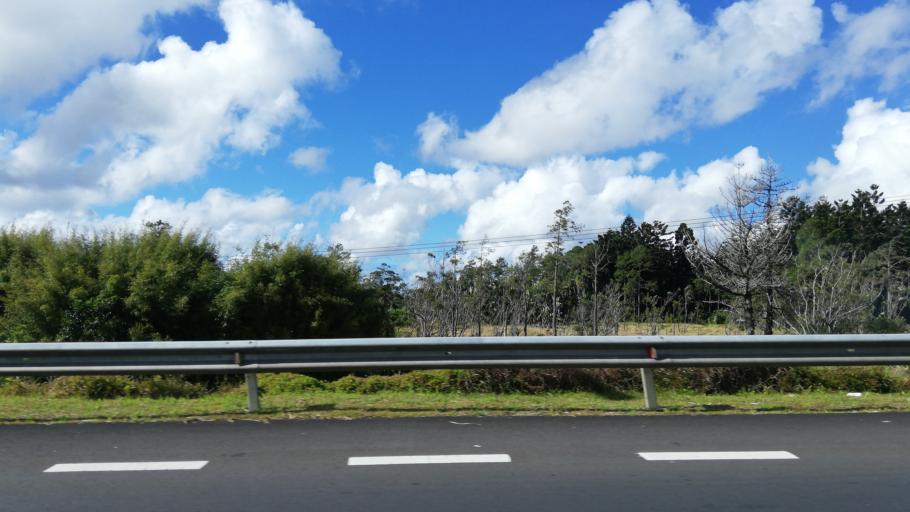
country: MU
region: Moka
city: Quartier Militaire
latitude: -20.2549
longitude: 57.5825
